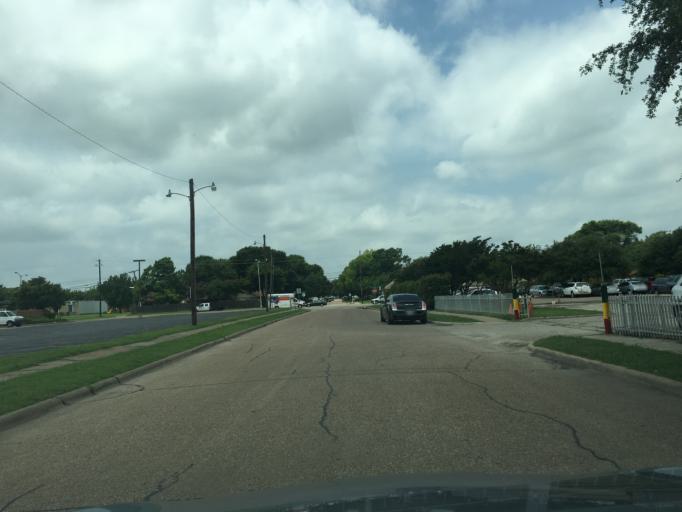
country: US
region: Texas
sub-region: Dallas County
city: Garland
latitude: 32.9210
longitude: -96.6818
